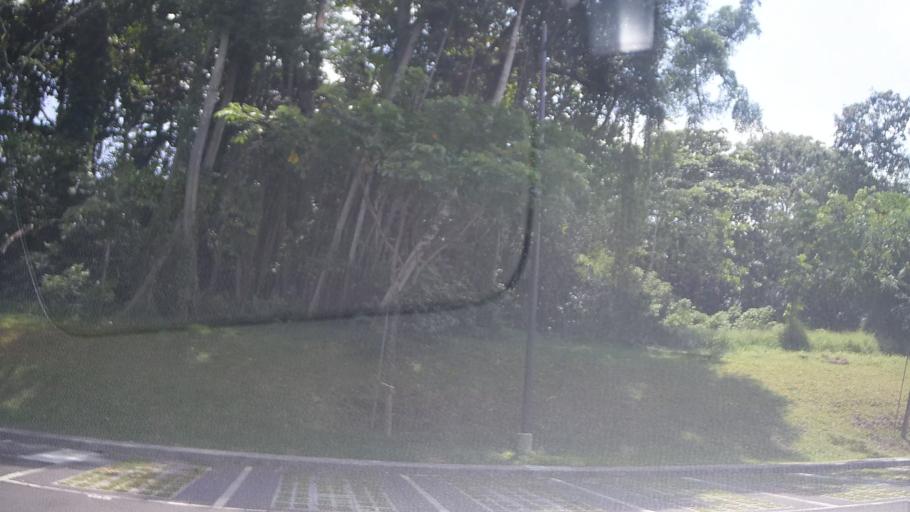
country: MY
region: Johor
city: Kampung Pasir Gudang Baru
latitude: 1.3995
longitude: 103.8729
